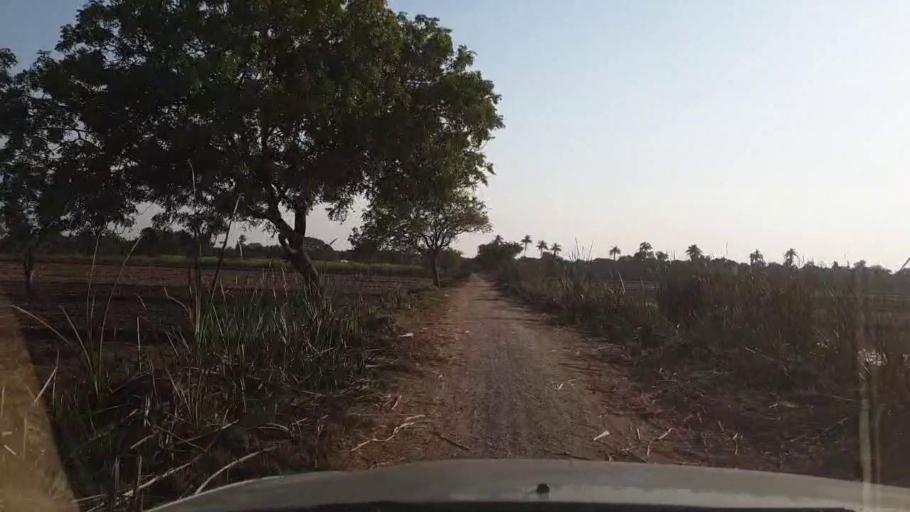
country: PK
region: Sindh
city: Tando Muhammad Khan
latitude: 25.1257
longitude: 68.5526
